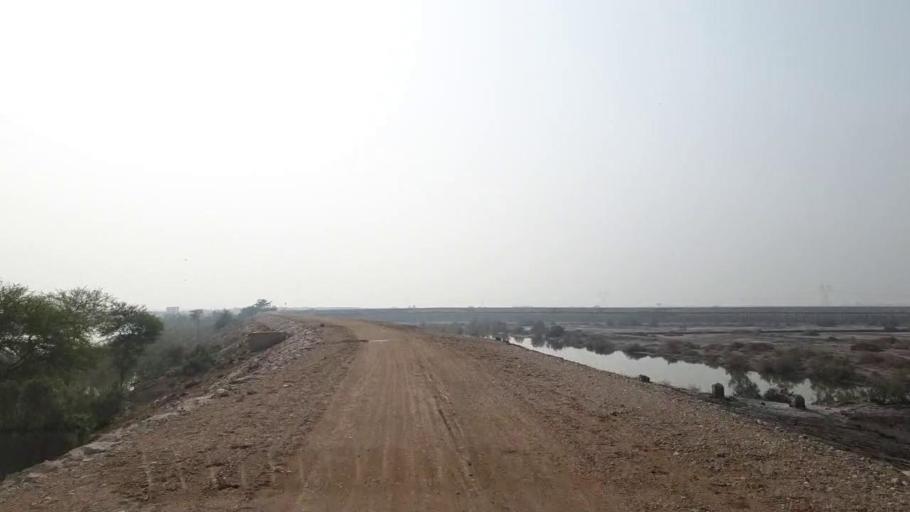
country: PK
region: Sindh
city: Sehwan
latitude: 26.4017
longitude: 67.8306
